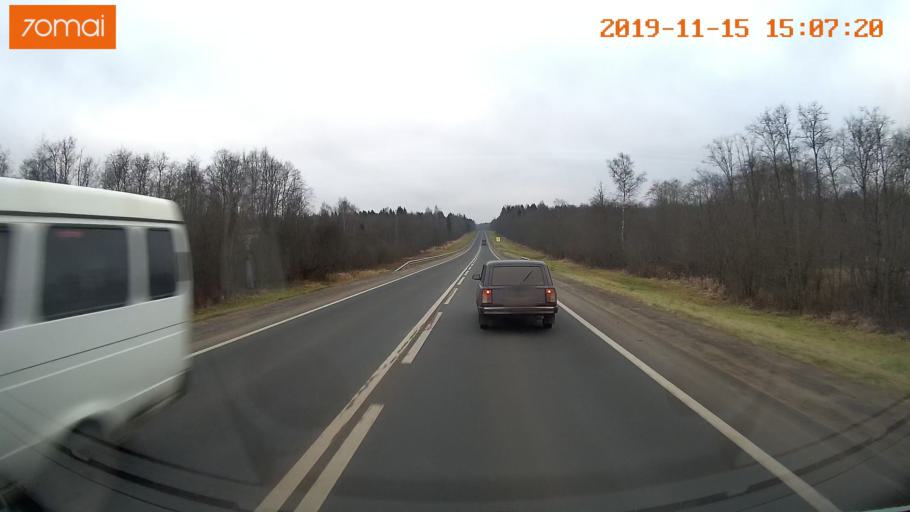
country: RU
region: Jaroslavl
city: Prechistoye
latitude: 58.3848
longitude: 40.2974
